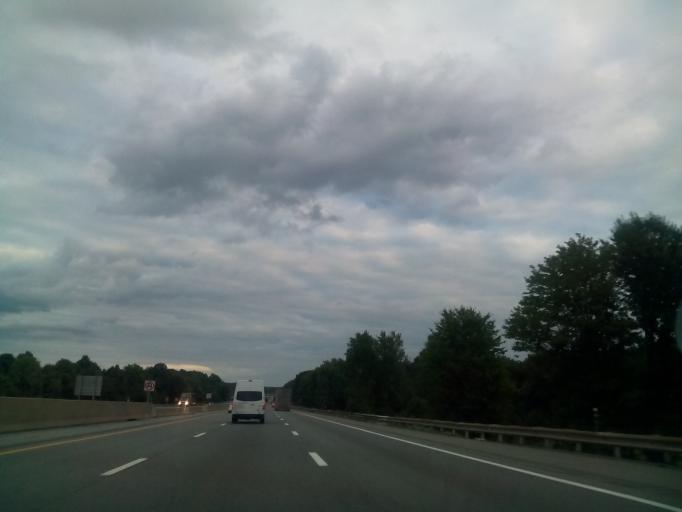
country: US
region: Ohio
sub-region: Trumbull County
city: Newton Falls
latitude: 41.1843
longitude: -80.9315
